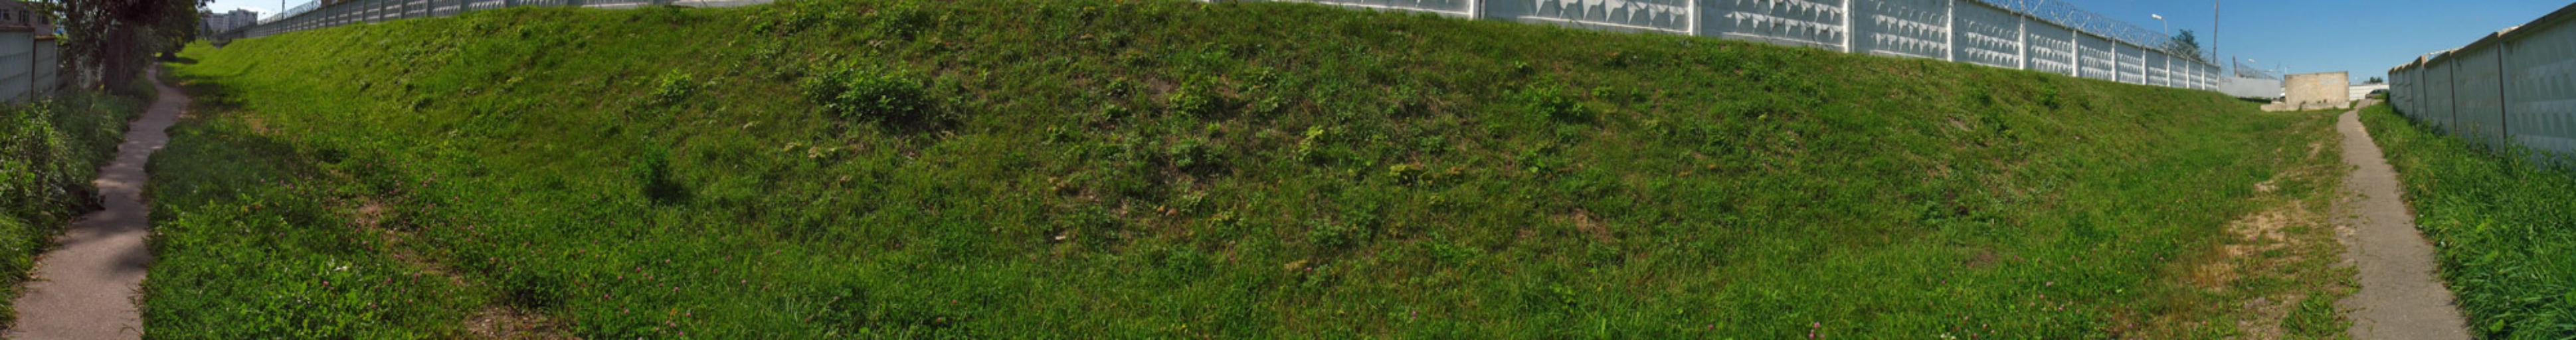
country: BY
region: Minsk
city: Vyaliki Trastsyanets
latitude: 53.8632
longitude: 27.6922
